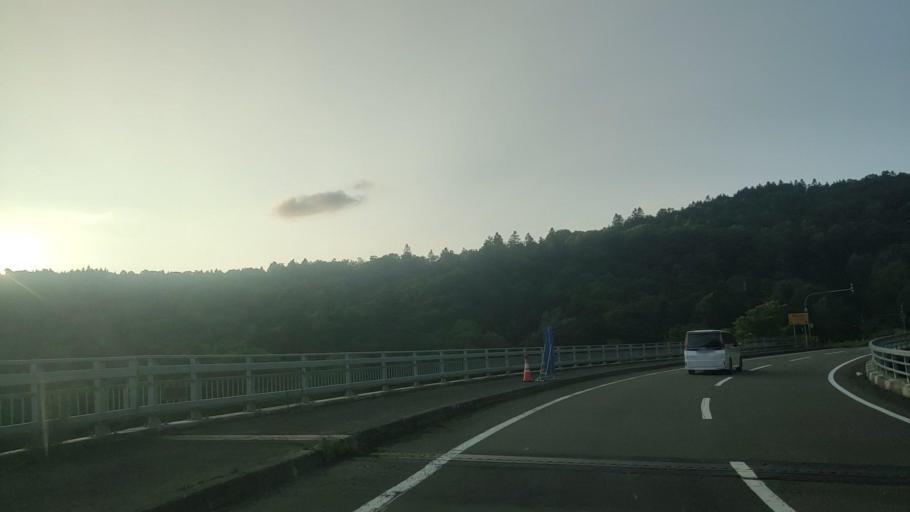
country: JP
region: Hokkaido
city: Bibai
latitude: 43.2365
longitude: 142.0301
